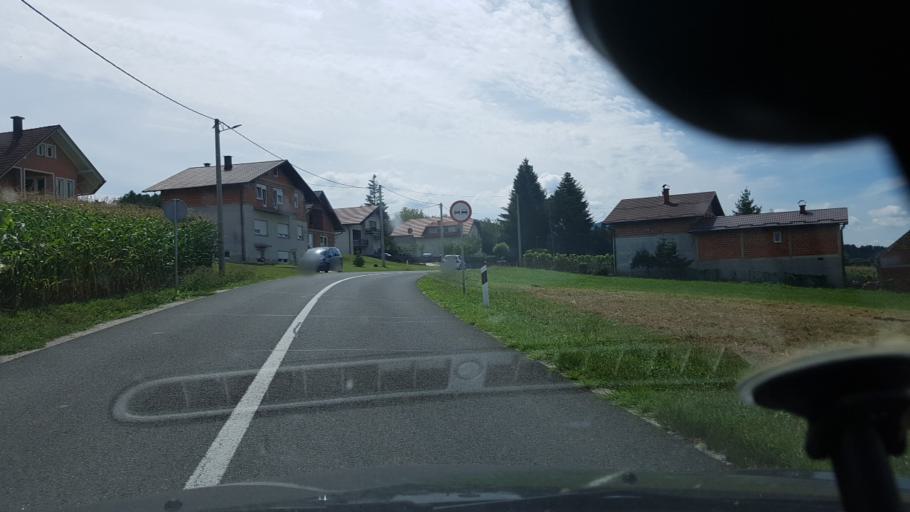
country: HR
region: Varazdinska
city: Lepoglava
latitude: 46.2239
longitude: 15.9771
